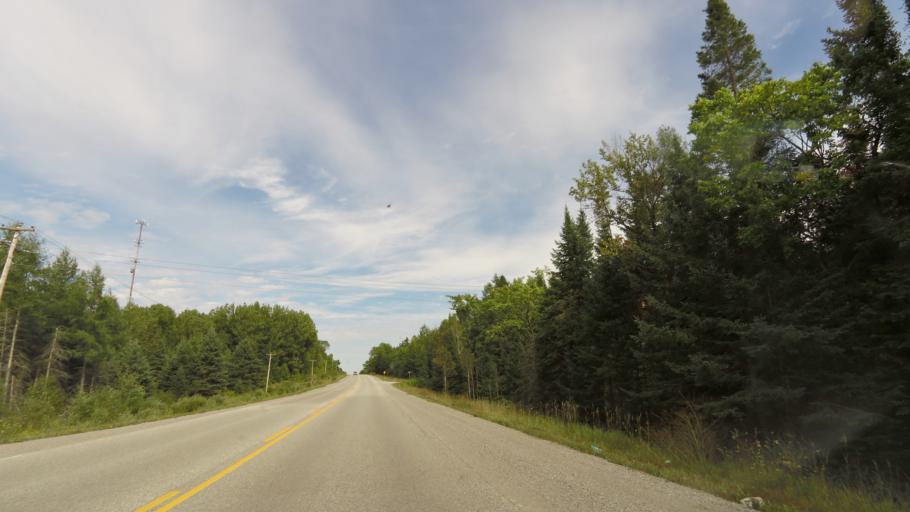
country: CA
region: Ontario
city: Omemee
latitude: 44.6573
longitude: -78.8285
